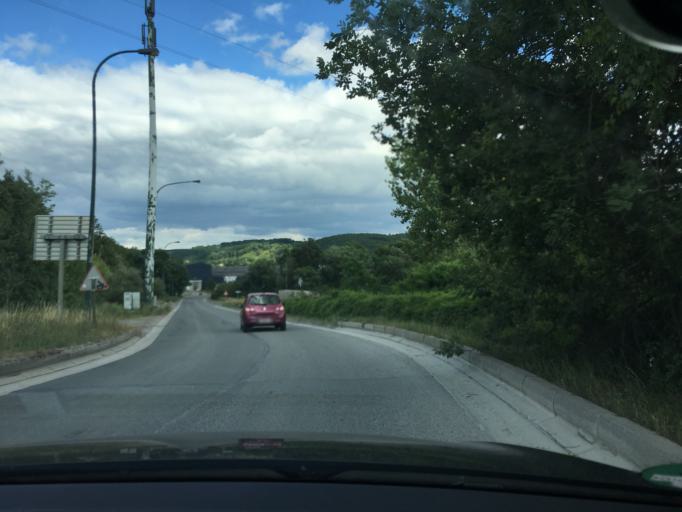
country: BE
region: Wallonia
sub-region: Province de Liege
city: Engis
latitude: 50.5627
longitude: 5.3560
